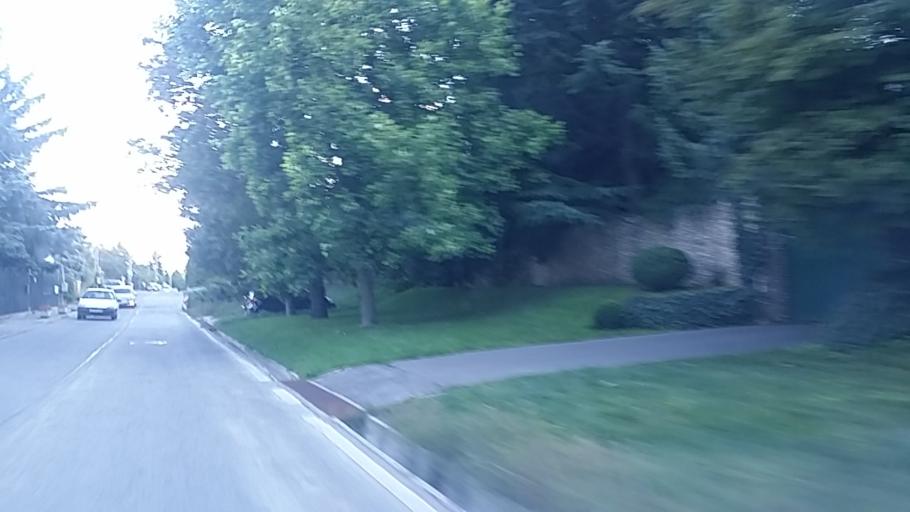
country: HU
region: Budapest
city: Budapest III. keruelet
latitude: 47.5569
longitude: 19.0170
